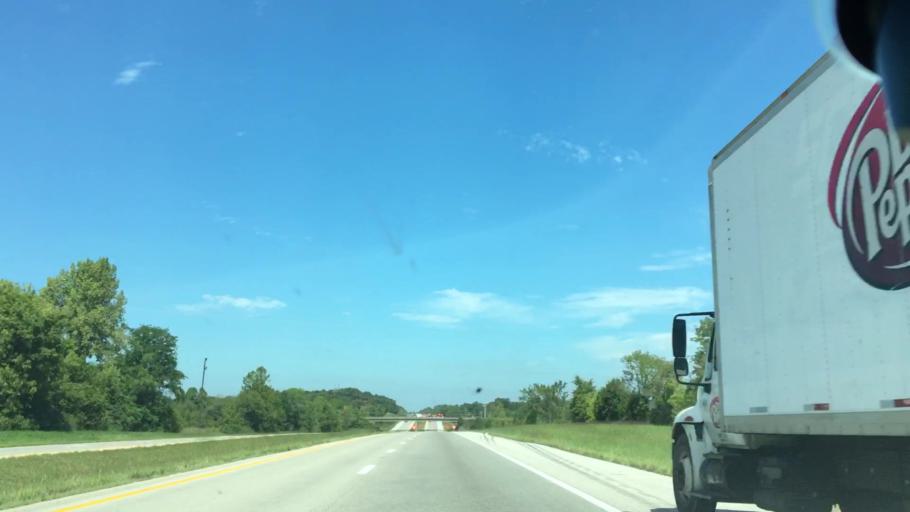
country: US
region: Kentucky
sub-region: Christian County
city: Hopkinsville
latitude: 36.9442
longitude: -87.4686
